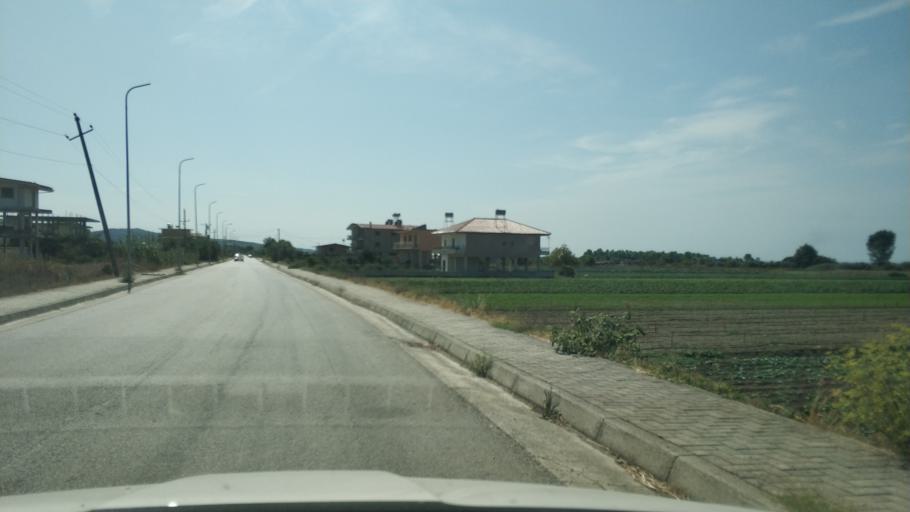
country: AL
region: Fier
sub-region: Rrethi i Lushnjes
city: Divjake
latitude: 40.9848
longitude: 19.5343
